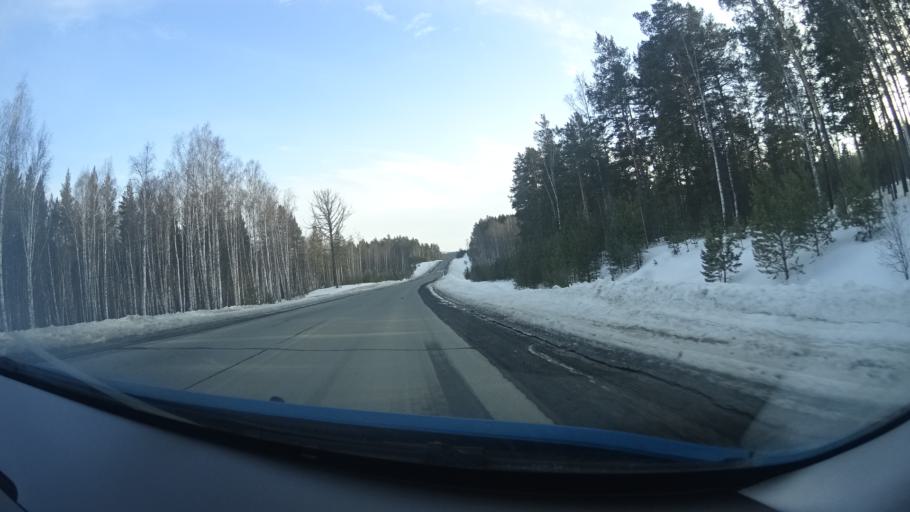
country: RU
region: Bashkortostan
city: Lomovka
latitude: 53.4795
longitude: 58.3153
